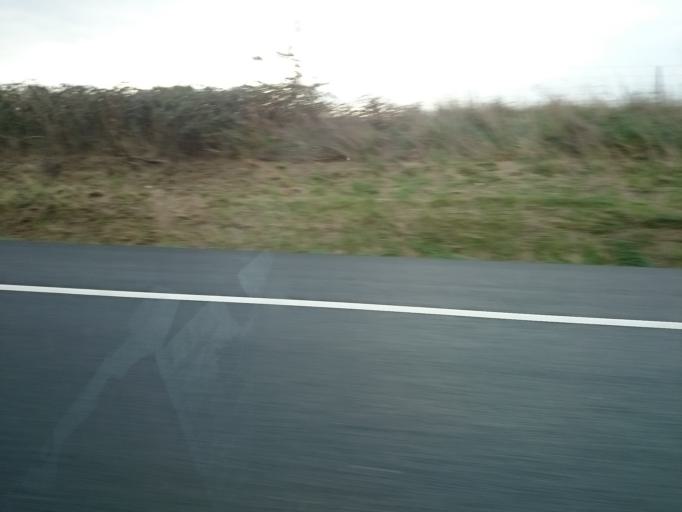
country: FR
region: Brittany
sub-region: Departement d'Ille-et-Vilaine
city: Pleumeleuc
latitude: 48.1732
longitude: -1.9167
